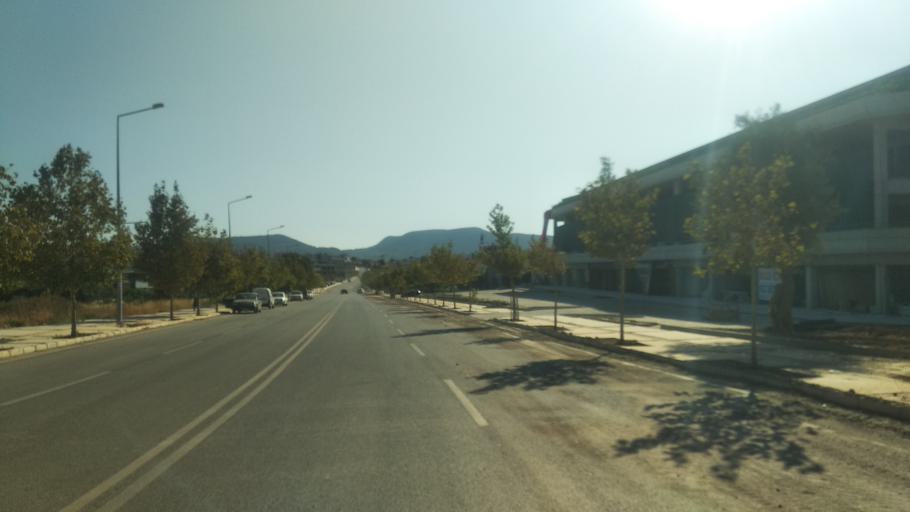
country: TR
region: Izmir
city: Urla
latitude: 38.3588
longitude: 26.8756
